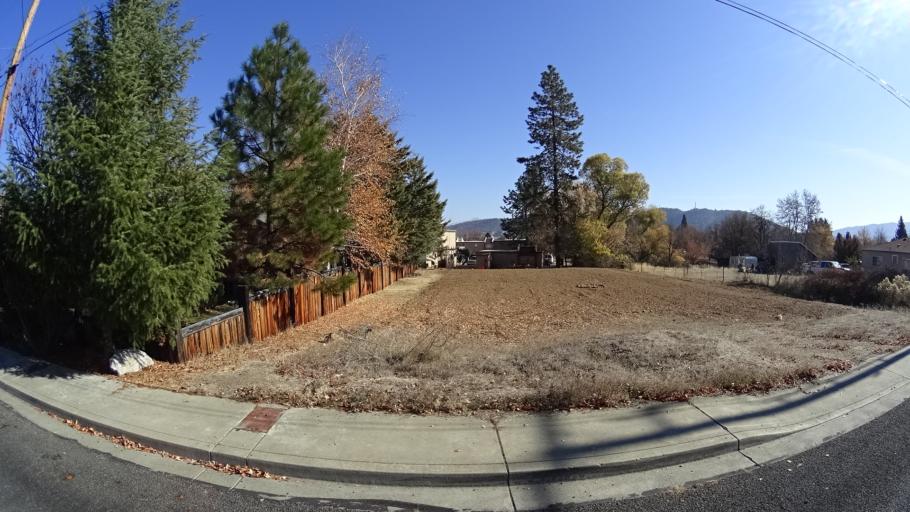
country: US
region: California
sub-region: Siskiyou County
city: Yreka
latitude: 41.7341
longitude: -122.6510
